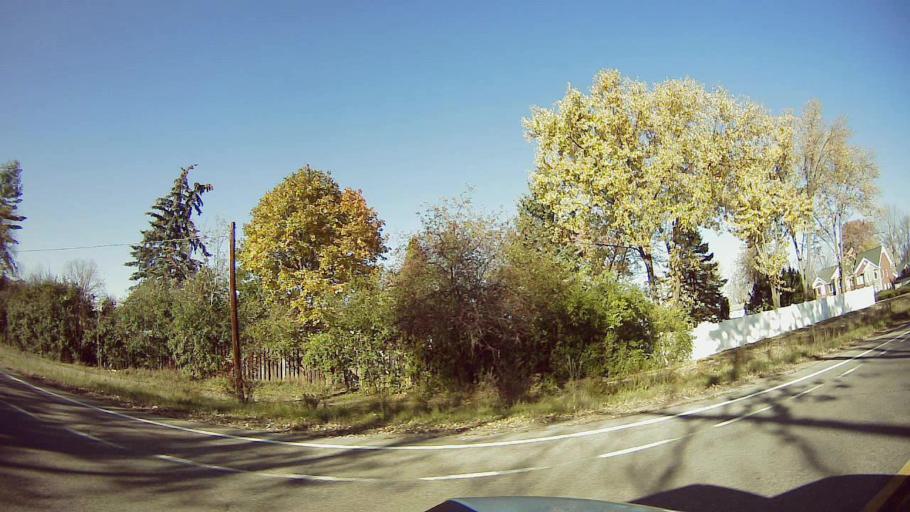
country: US
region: Michigan
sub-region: Oakland County
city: Orchard Lake
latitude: 42.5434
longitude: -83.3438
